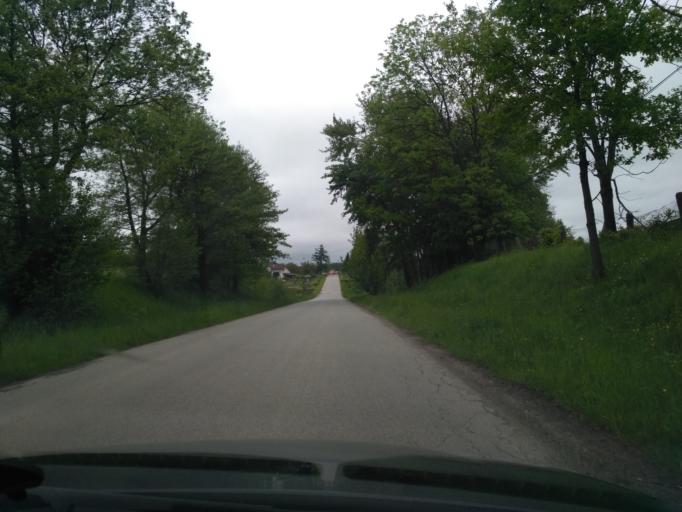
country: PL
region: Subcarpathian Voivodeship
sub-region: Powiat jasielski
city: Brzyska
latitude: 49.8370
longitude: 21.3915
